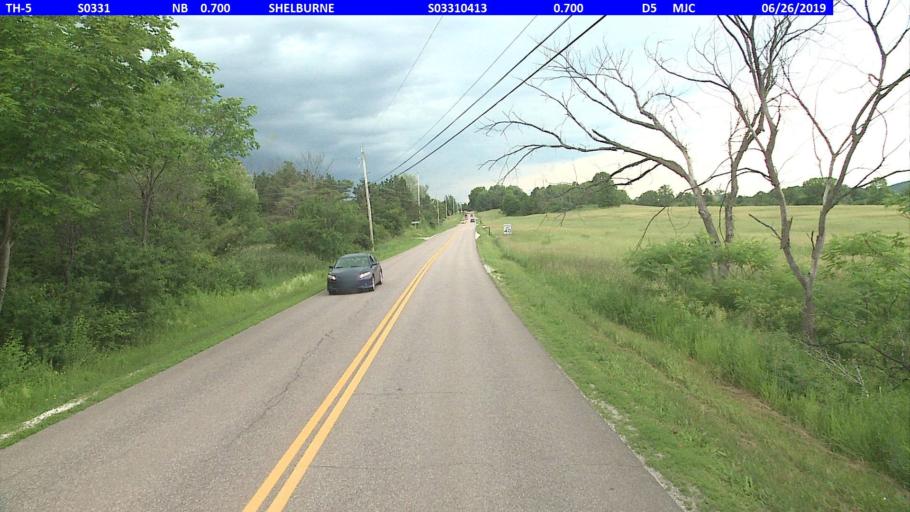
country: US
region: Vermont
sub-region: Chittenden County
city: Hinesburg
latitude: 44.3812
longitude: -73.1779
